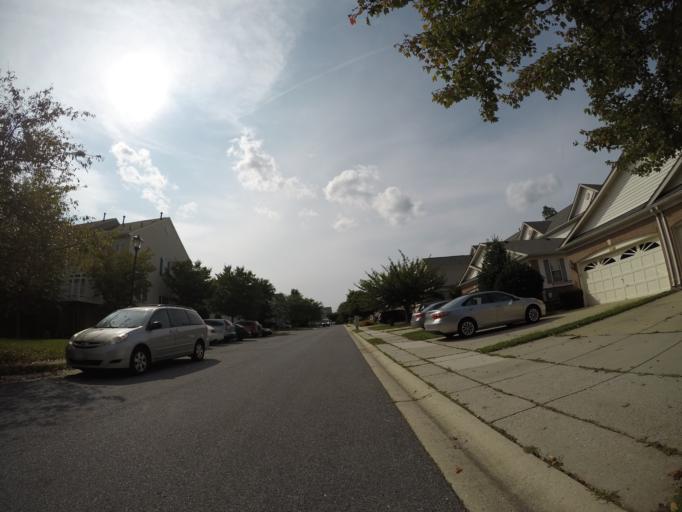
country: US
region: Maryland
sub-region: Howard County
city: Columbia
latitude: 39.3105
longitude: -76.8875
